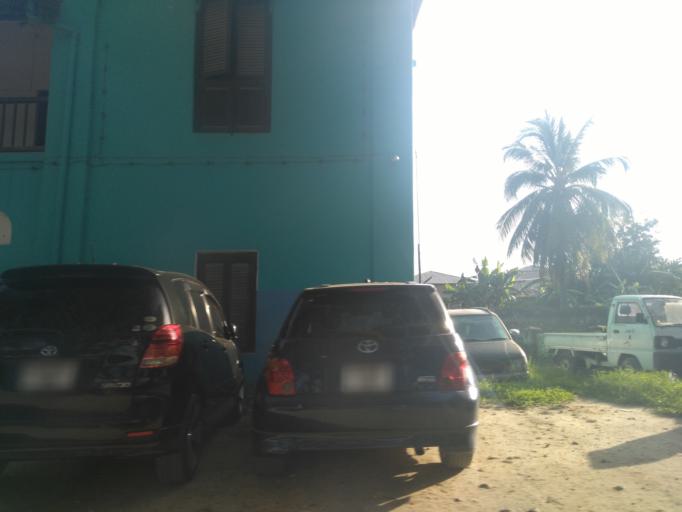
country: TZ
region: Zanzibar Urban/West
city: Zanzibar
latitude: -6.1685
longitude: 39.1942
